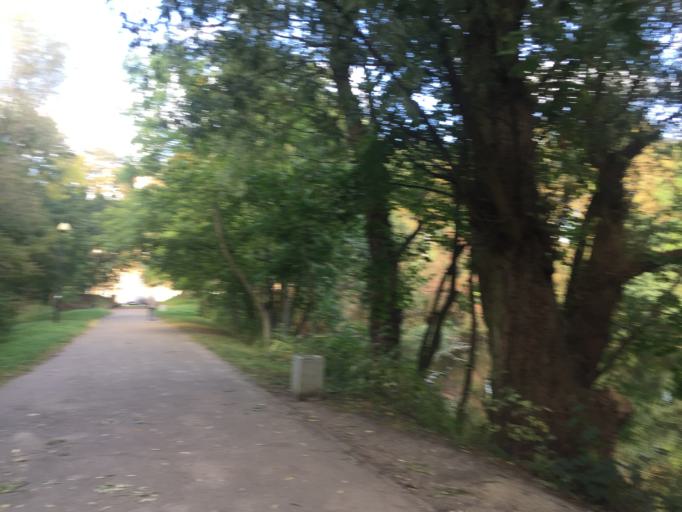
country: RU
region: Kaliningrad
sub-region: Gorod Kaliningrad
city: Kaliningrad
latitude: 54.6940
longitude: 20.5071
